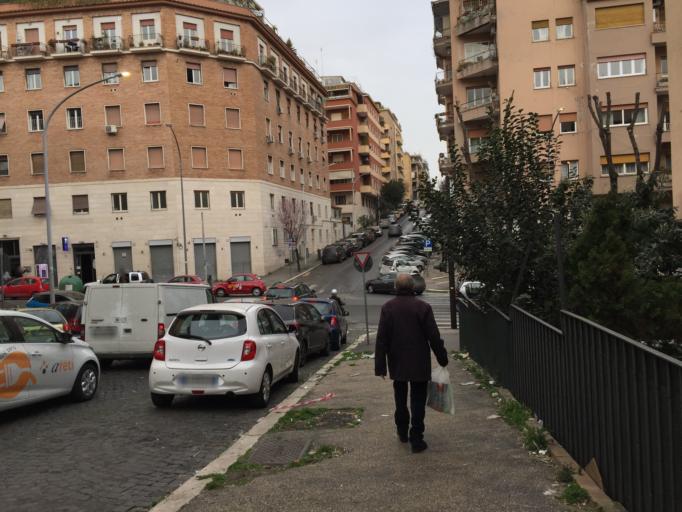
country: VA
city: Vatican City
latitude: 41.8827
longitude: 12.4582
